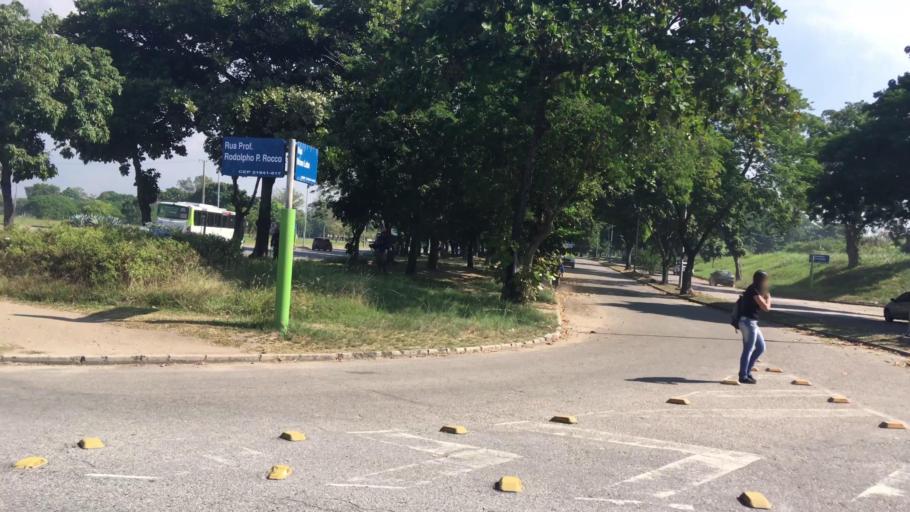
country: BR
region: Rio de Janeiro
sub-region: Rio De Janeiro
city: Rio de Janeiro
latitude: -22.8433
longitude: -43.2346
